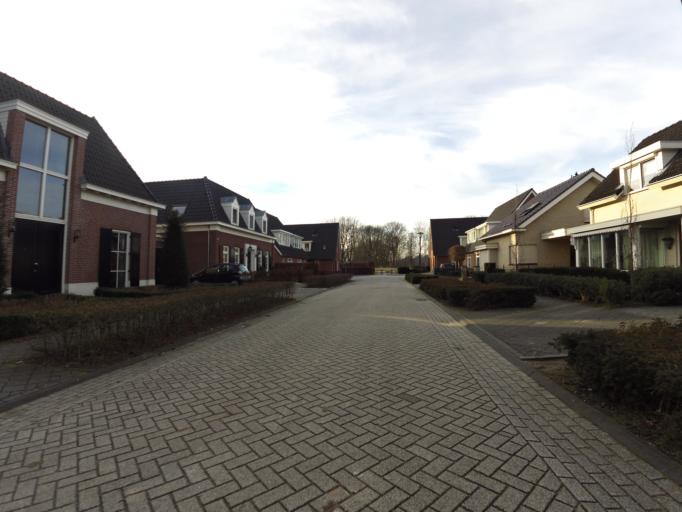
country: NL
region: Gelderland
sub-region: Gemeente Montferland
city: s-Heerenberg
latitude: 51.8698
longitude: 6.2494
